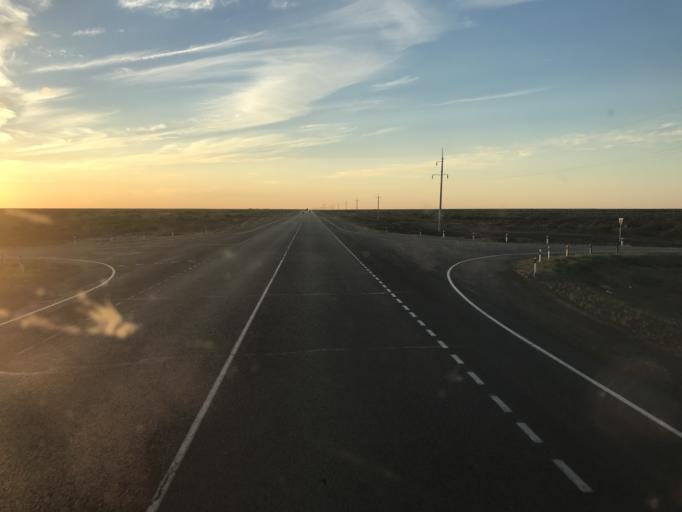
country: KZ
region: Qyzylorda
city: Zhosaly
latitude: 45.2452
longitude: 64.1184
